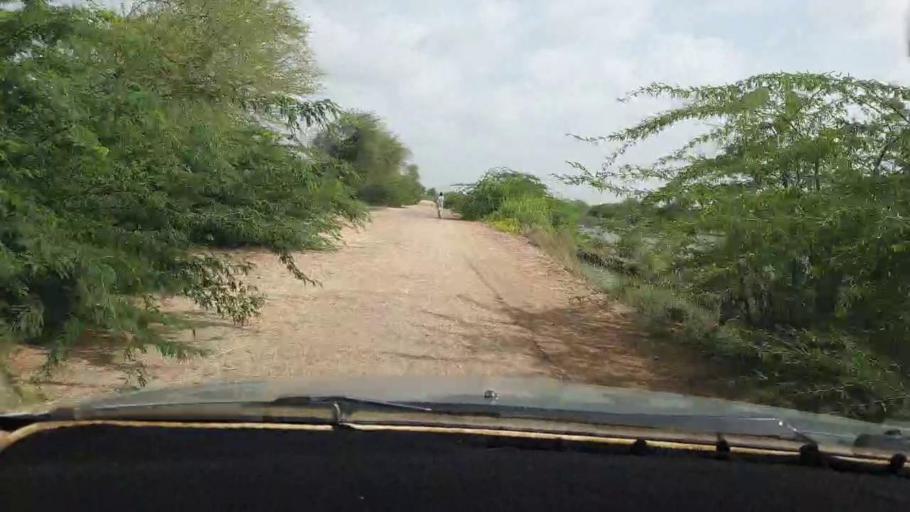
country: PK
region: Sindh
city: Tando Bago
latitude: 24.7795
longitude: 69.0265
